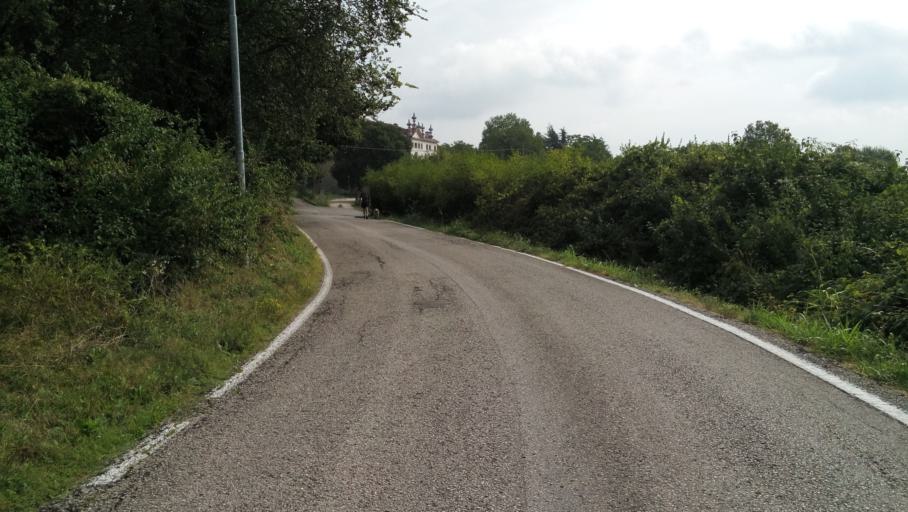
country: IT
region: Veneto
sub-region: Provincia di Vicenza
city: Creazzo
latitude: 45.5445
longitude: 11.4737
